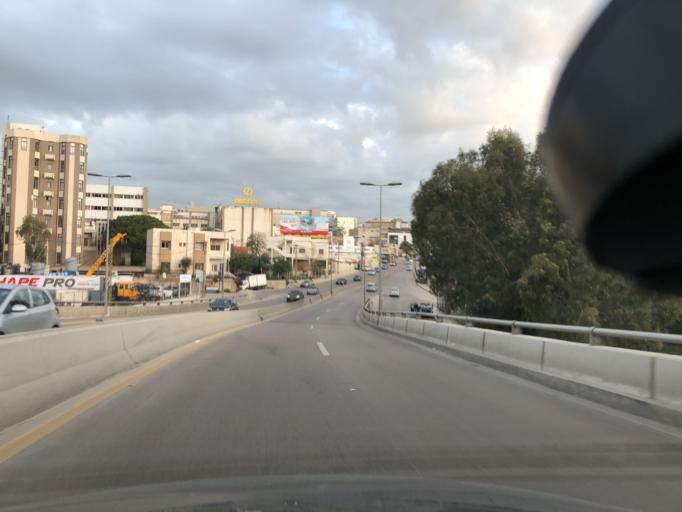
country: LB
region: Mont-Liban
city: Jdaidet el Matn
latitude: 33.8688
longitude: 35.5430
